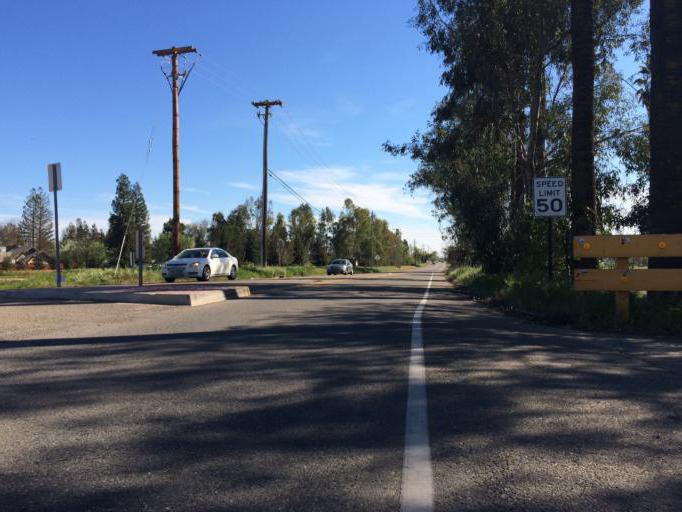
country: US
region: California
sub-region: Fresno County
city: Clovis
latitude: 36.8640
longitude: -119.6841
